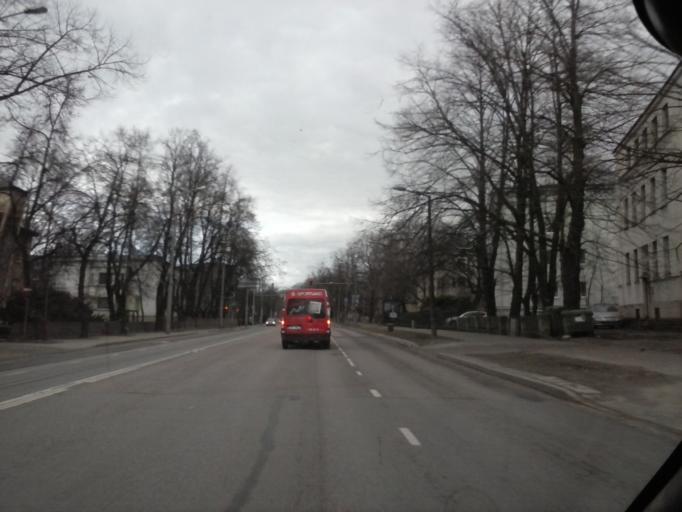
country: EE
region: Harju
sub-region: Tallinna linn
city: Tallinn
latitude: 59.4395
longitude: 24.7784
